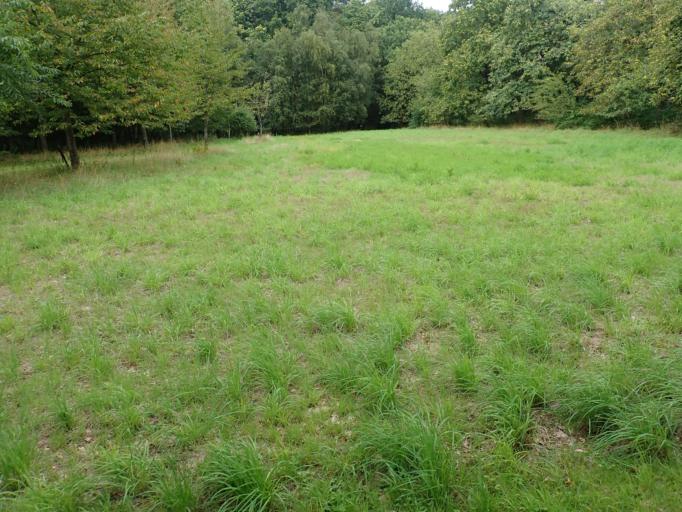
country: BE
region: Flanders
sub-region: Provincie Antwerpen
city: Puurs
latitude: 51.0729
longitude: 4.3098
